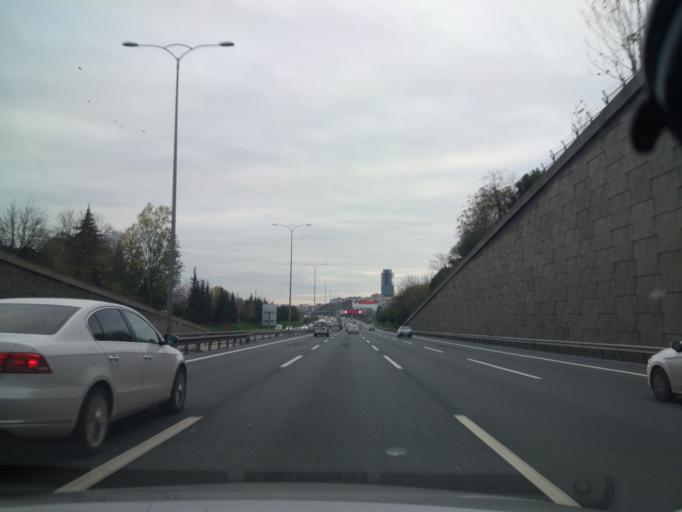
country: TR
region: Istanbul
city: Sisli
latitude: 41.0960
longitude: 29.0178
